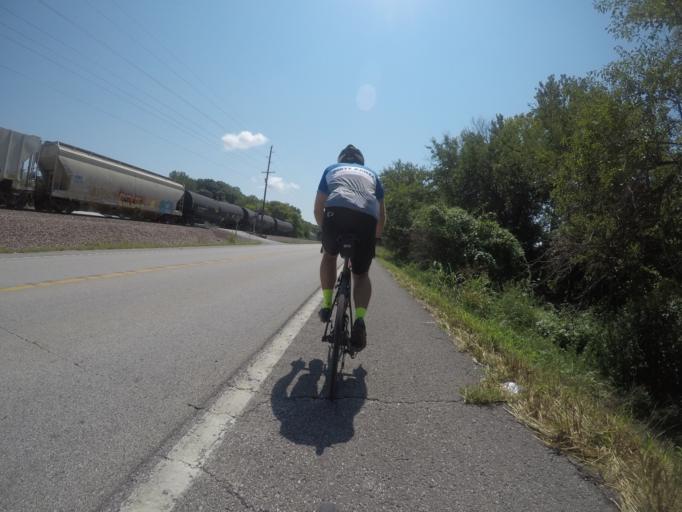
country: US
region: Missouri
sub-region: Platte County
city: Weston
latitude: 39.4743
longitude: -94.9844
